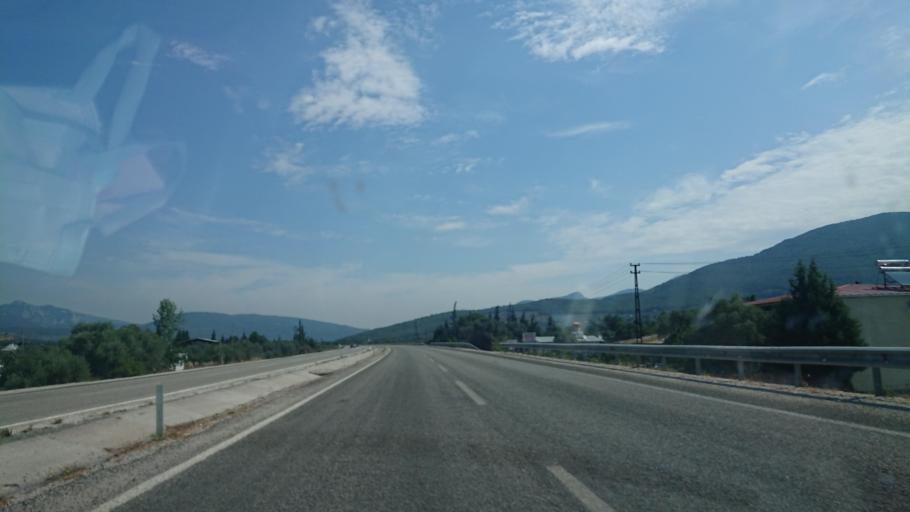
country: TR
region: Izmir
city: Dagkizilca
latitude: 38.2919
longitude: 27.4059
